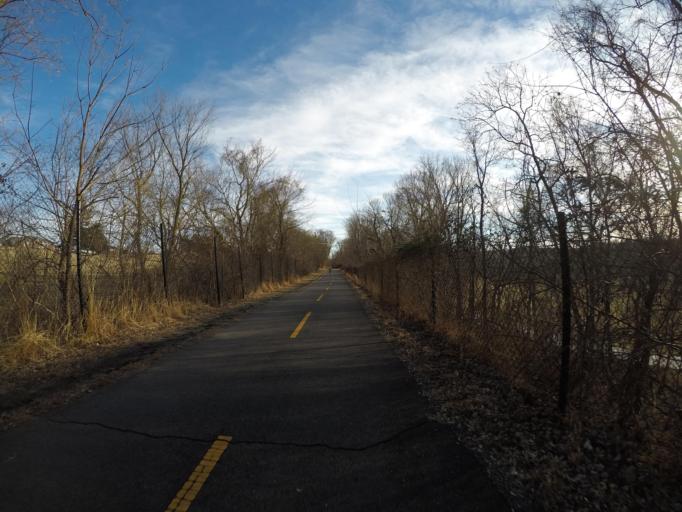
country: US
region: Virginia
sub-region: Loudoun County
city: Leesburg
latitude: 39.1209
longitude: -77.6043
